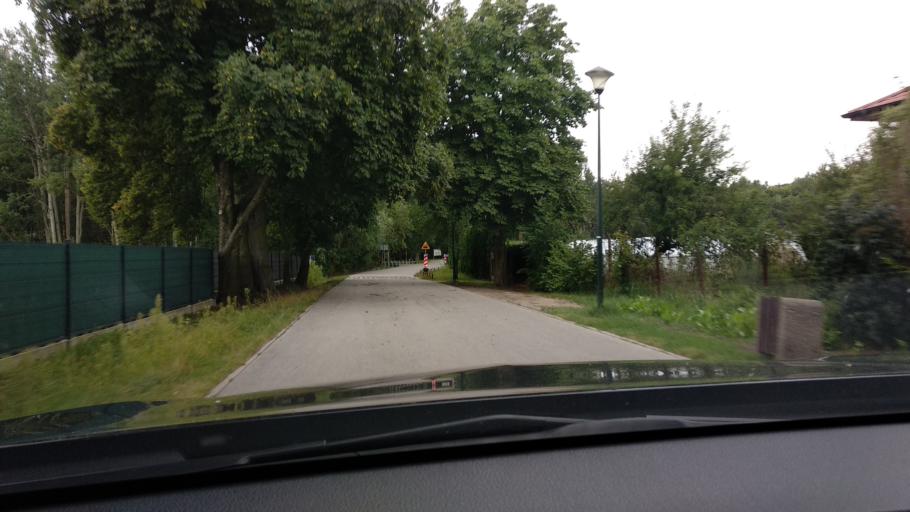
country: PL
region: Masovian Voivodeship
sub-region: Warszawa
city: Ursynow
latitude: 52.1317
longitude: 21.0463
